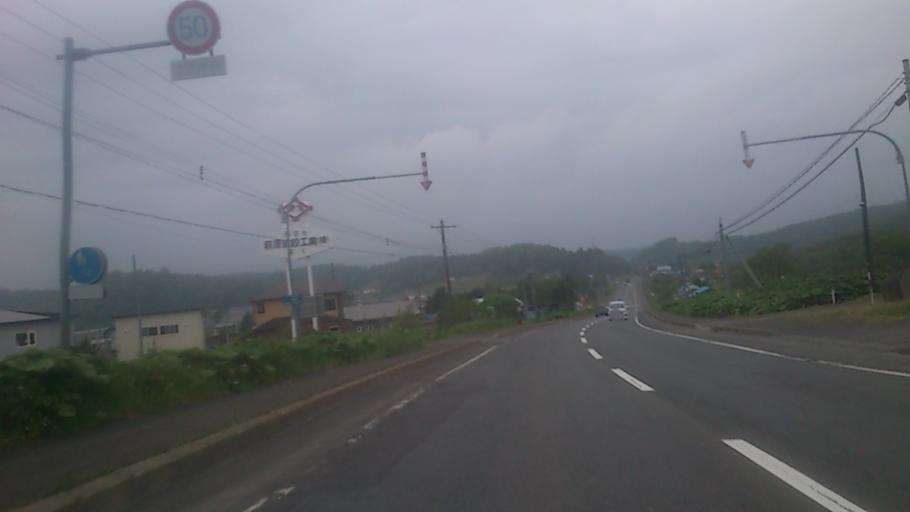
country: JP
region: Hokkaido
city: Kushiro
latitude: 43.0579
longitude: 144.7914
